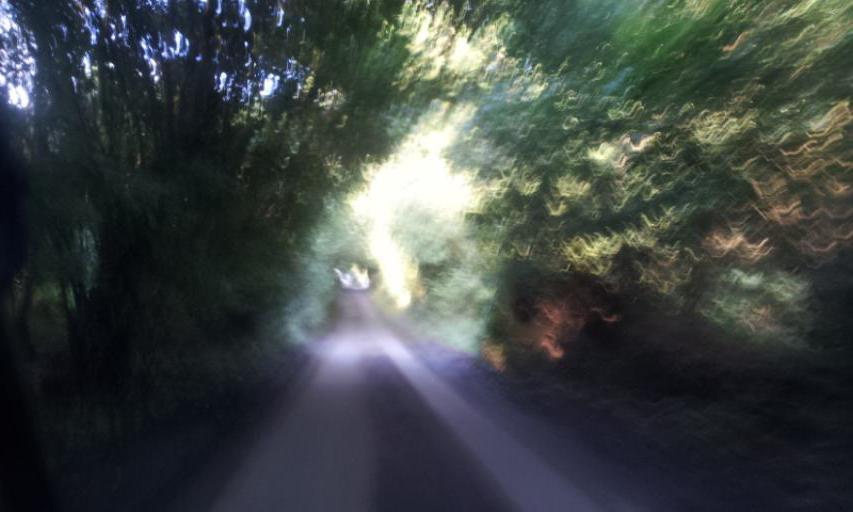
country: GB
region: England
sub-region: Kent
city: Meopham
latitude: 51.3869
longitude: 0.3723
